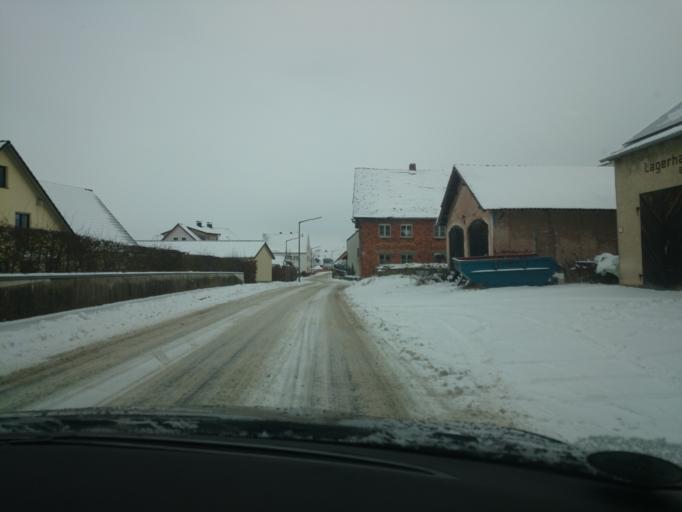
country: DE
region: Bavaria
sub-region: Regierungsbezirk Mittelfranken
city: Thalmassing
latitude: 49.1321
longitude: 11.2150
